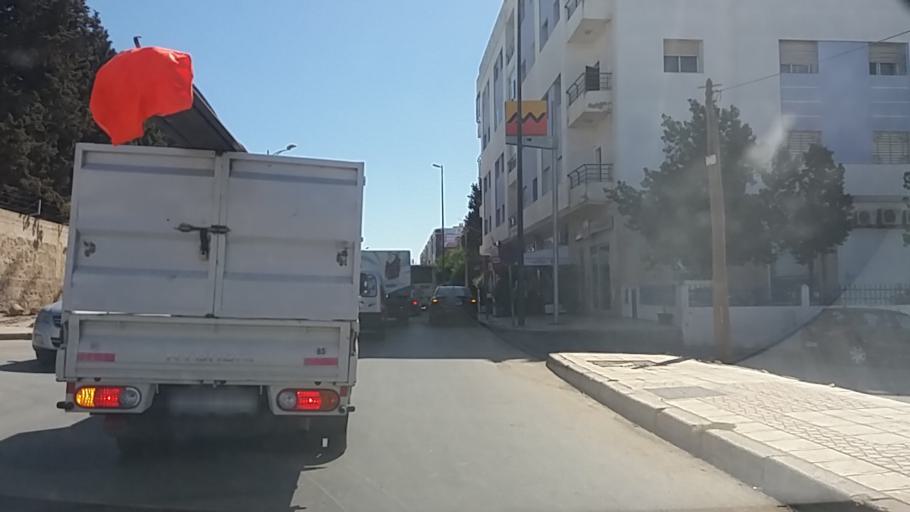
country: MA
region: Gharb-Chrarda-Beni Hssen
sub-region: Kenitra Province
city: Kenitra
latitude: 34.2417
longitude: -6.6144
